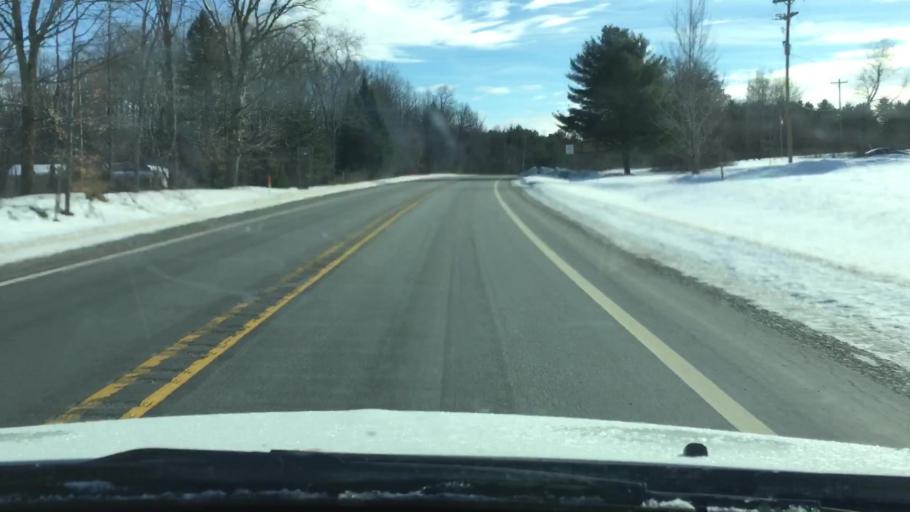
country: US
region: Michigan
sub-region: Antrim County
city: Mancelona
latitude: 44.9847
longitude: -85.0548
